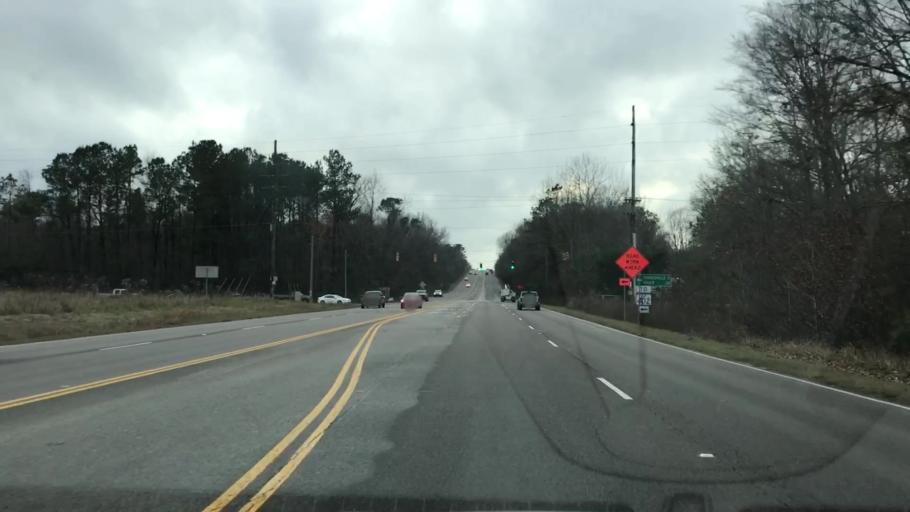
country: US
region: South Carolina
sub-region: Berkeley County
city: Moncks Corner
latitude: 33.2196
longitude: -79.9687
